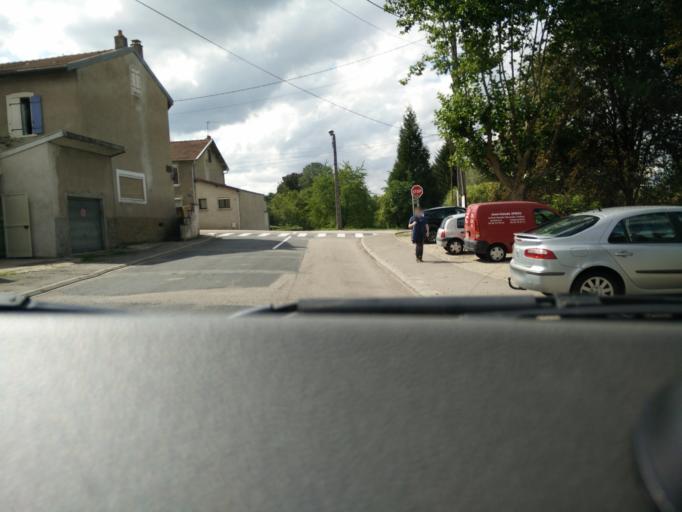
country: FR
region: Lorraine
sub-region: Departement de Meurthe-et-Moselle
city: Damelevieres
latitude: 48.5571
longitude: 6.4020
